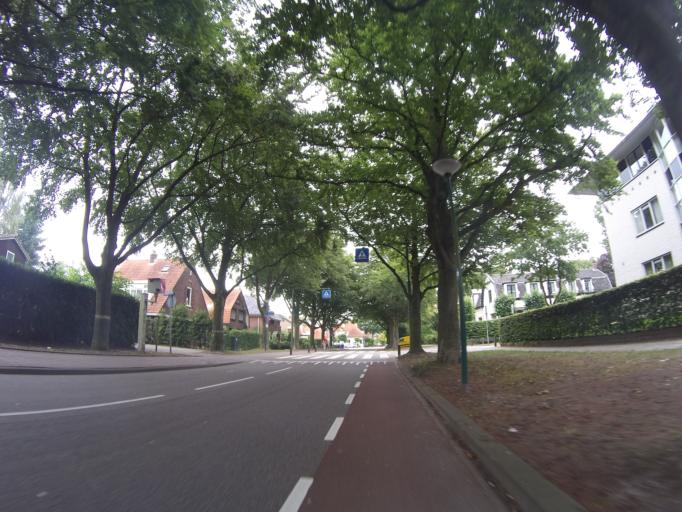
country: NL
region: Utrecht
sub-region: Gemeente Baarn
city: Baarn
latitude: 52.2186
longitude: 5.2687
